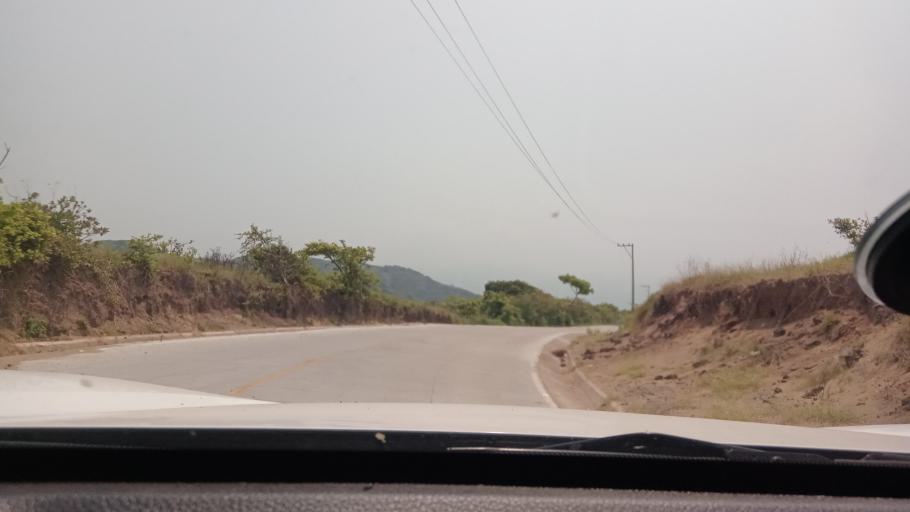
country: MX
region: Veracruz
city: Catemaco
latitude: 18.5563
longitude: -94.9963
